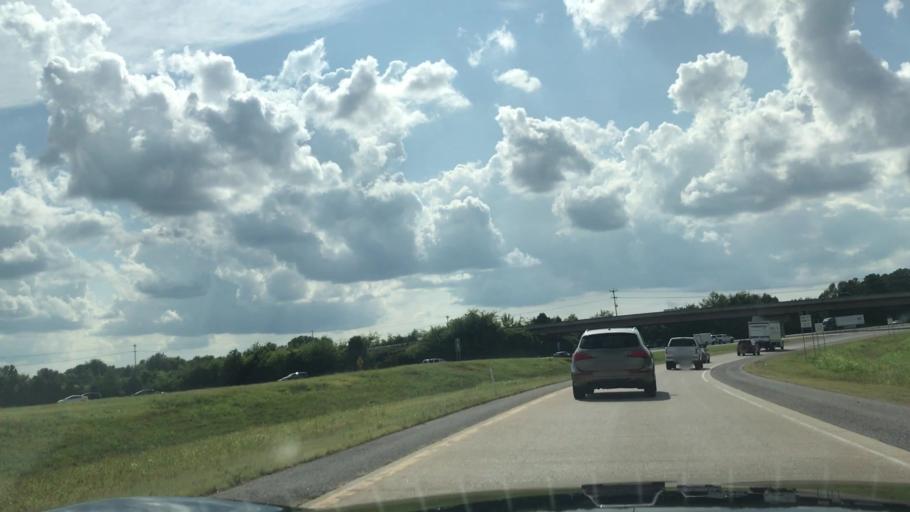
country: US
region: Tennessee
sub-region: Rutherford County
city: Murfreesboro
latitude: 35.8886
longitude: -86.4789
